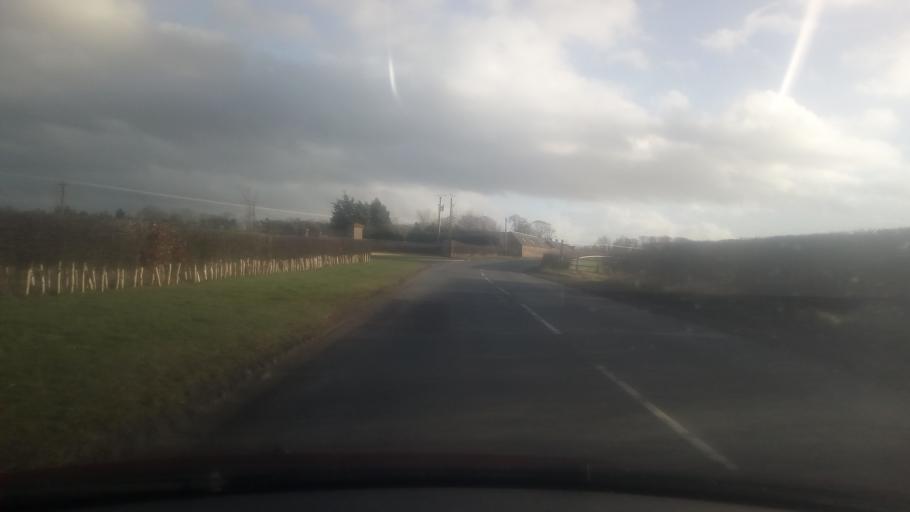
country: GB
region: Scotland
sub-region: The Scottish Borders
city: Kelso
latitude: 55.6140
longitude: -2.4259
